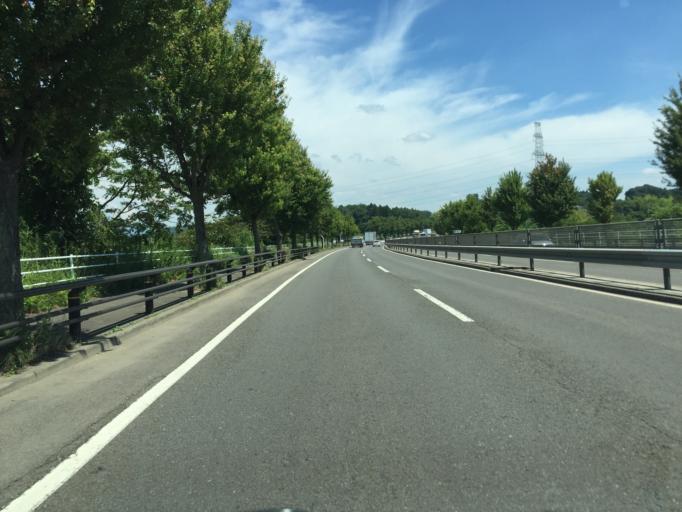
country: JP
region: Fukushima
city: Fukushima-shi
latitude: 37.6842
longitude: 140.4719
